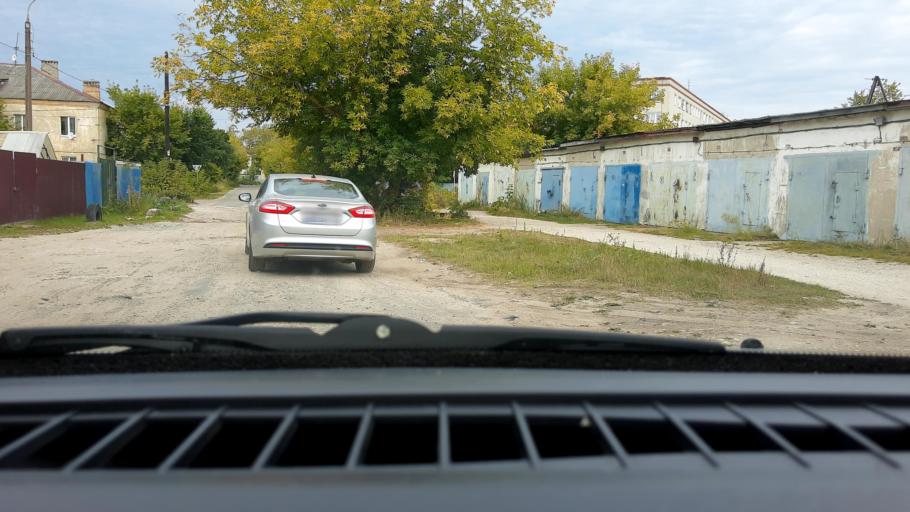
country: RU
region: Nizjnij Novgorod
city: Dzerzhinsk
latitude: 56.2483
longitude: 43.4794
